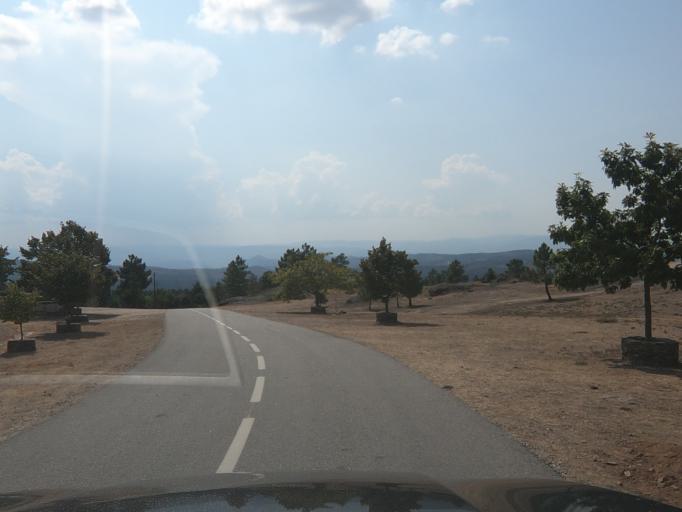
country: PT
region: Vila Real
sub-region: Sabrosa
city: Sabrosa
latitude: 41.2789
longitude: -7.6177
